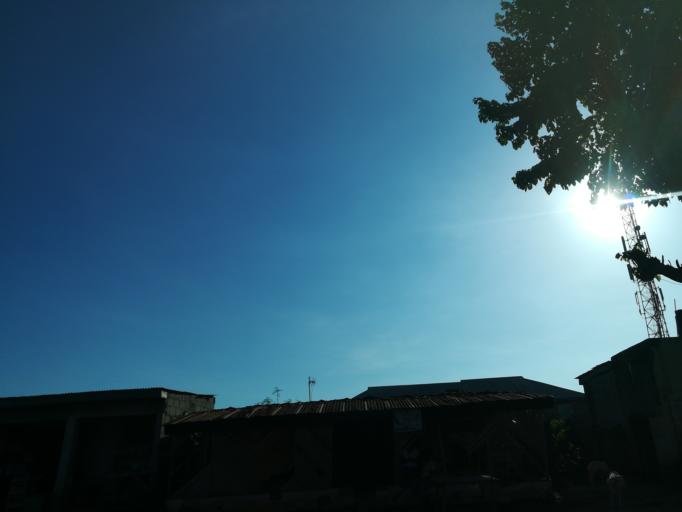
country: NG
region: Lagos
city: Ikorodu
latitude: 6.5585
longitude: 3.5378
